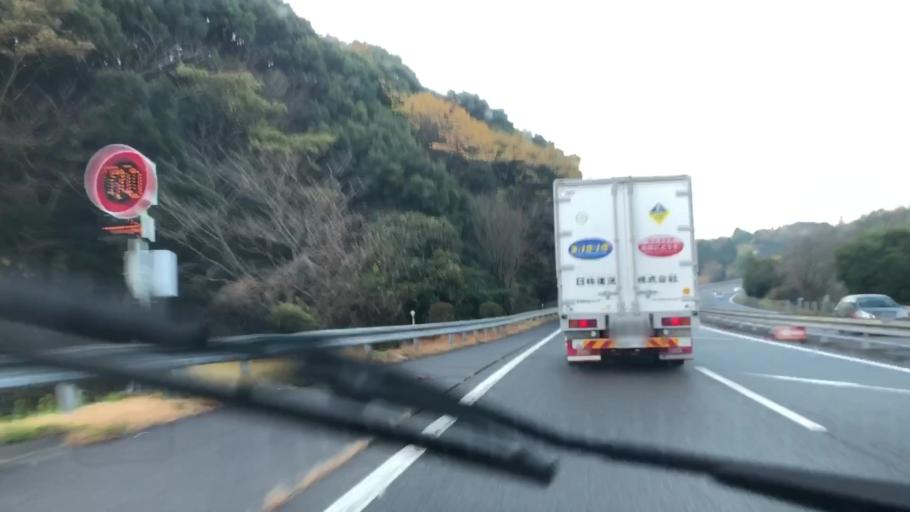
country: JP
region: Nagasaki
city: Sasebo
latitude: 33.1548
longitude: 129.8125
